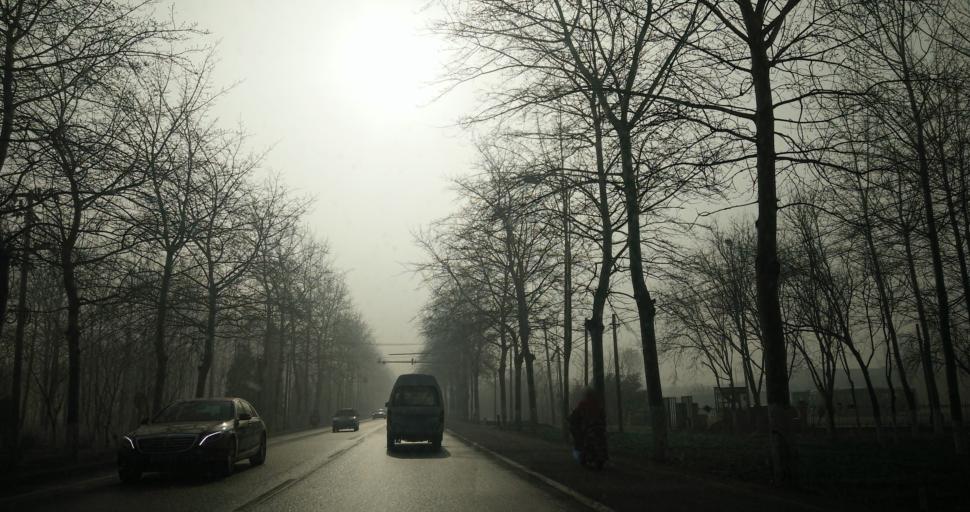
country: CN
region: Beijing
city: Yinghai
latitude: 39.7489
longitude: 116.4467
